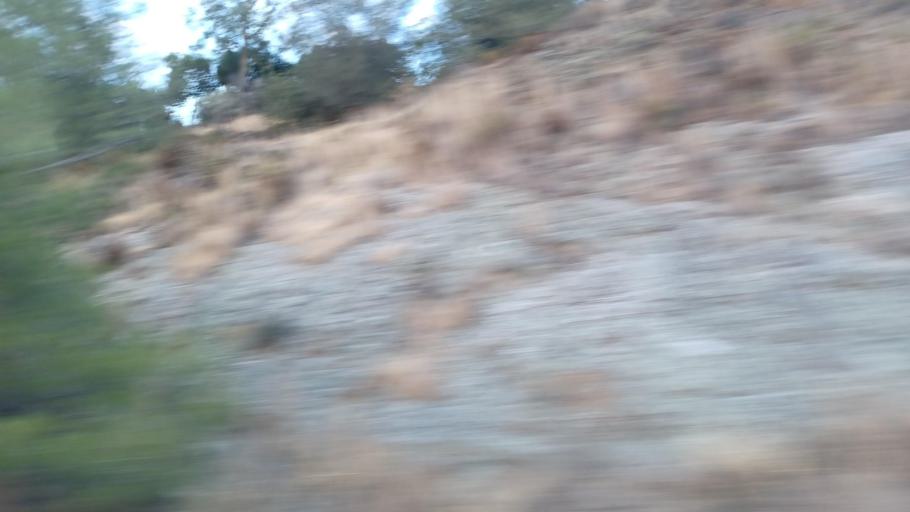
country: CY
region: Limassol
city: Pelendri
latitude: 34.8419
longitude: 32.9521
